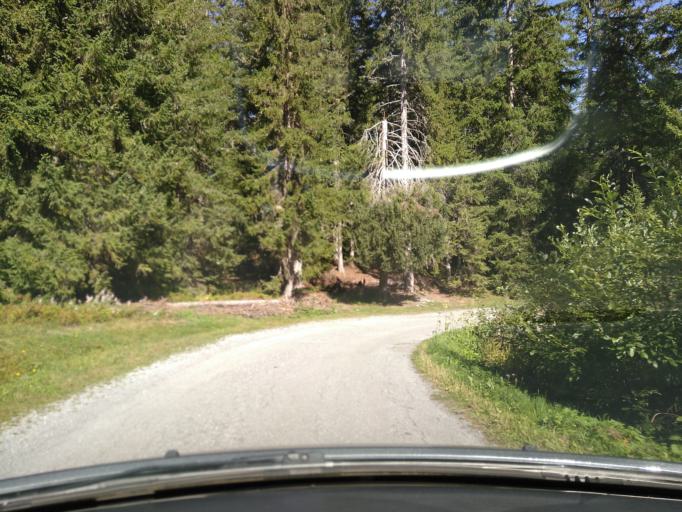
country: FR
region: Rhone-Alpes
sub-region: Departement de la Haute-Savoie
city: Praz-sur-Arly
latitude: 45.7812
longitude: 6.5265
